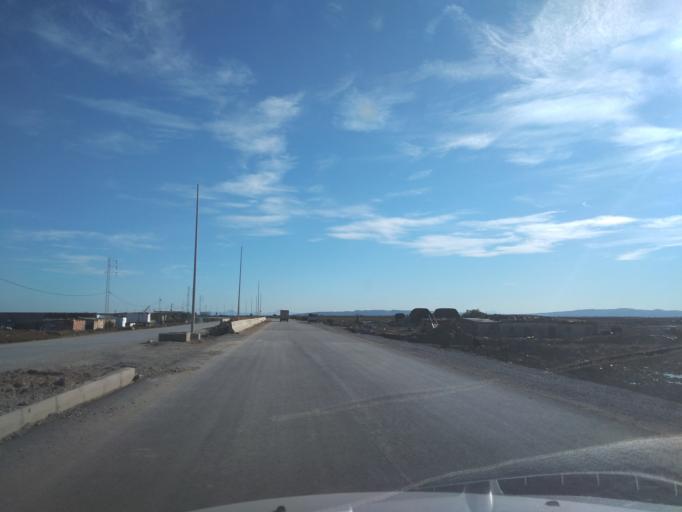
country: TN
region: Ariana
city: Qal'at al Andalus
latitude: 37.0493
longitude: 10.1239
